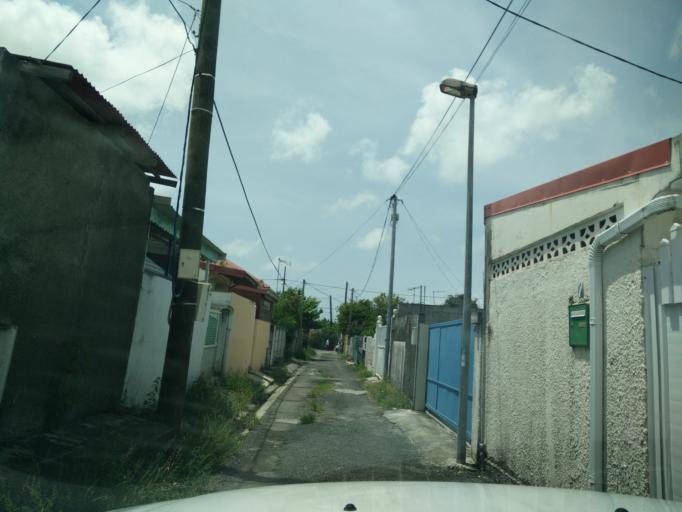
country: GP
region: Guadeloupe
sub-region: Guadeloupe
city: Pointe-a-Pitre
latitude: 16.2606
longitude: -61.5286
